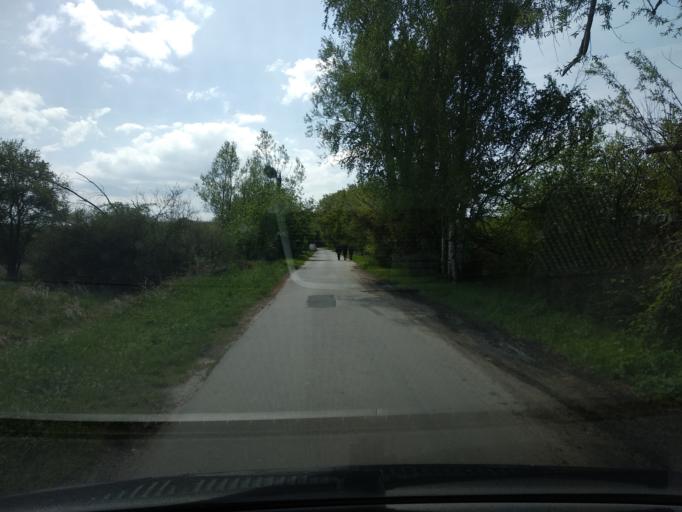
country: PL
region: Lower Silesian Voivodeship
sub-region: Powiat trzebnicki
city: Psary
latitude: 51.1616
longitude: 17.0781
